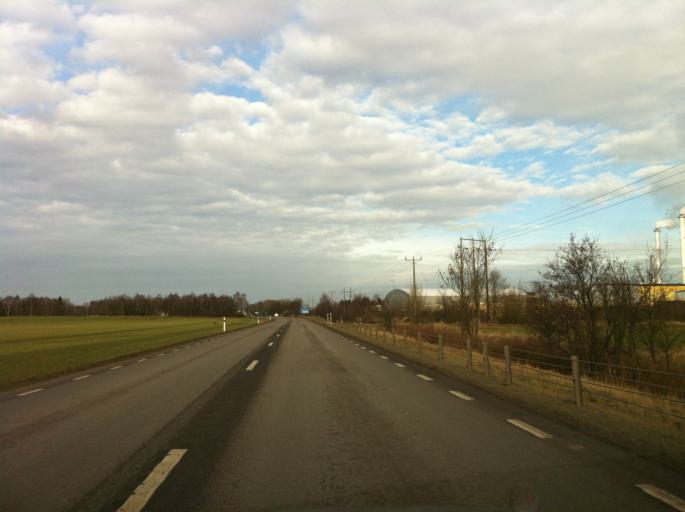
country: SE
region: Skane
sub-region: Bjuvs Kommun
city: Billesholm
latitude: 56.0459
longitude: 12.9680
